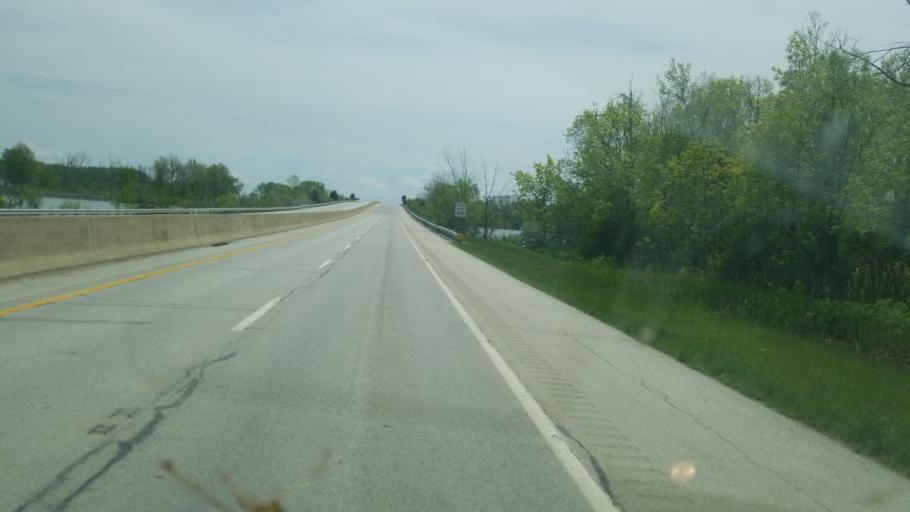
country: US
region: Ohio
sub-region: Ottawa County
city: Port Clinton
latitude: 41.5225
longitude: -83.0070
